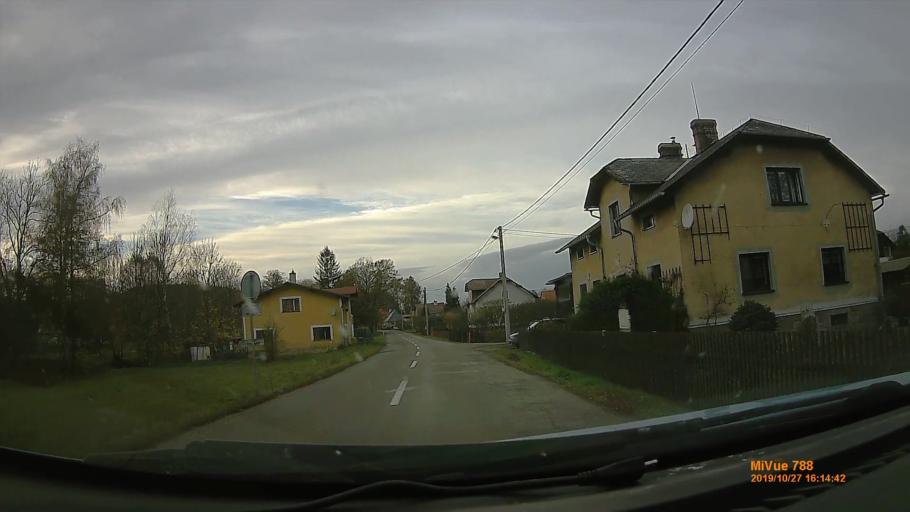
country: PL
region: Lower Silesian Voivodeship
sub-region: Powiat klodzki
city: Radkow
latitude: 50.5560
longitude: 16.3911
